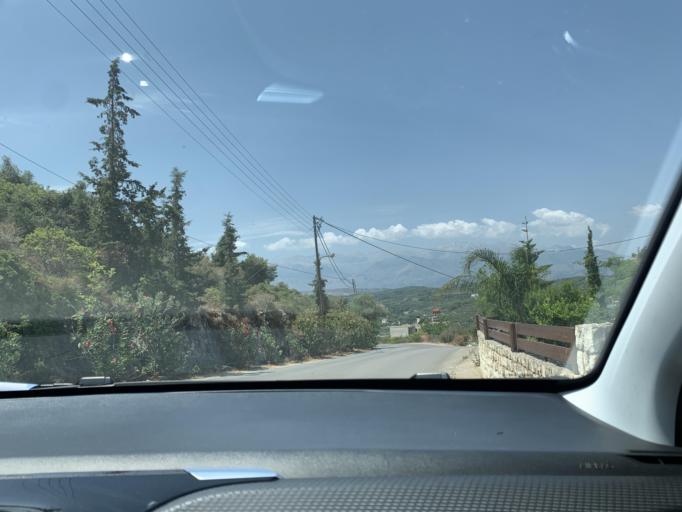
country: GR
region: Crete
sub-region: Nomos Chanias
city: Kalivai
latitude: 35.4494
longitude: 24.2072
